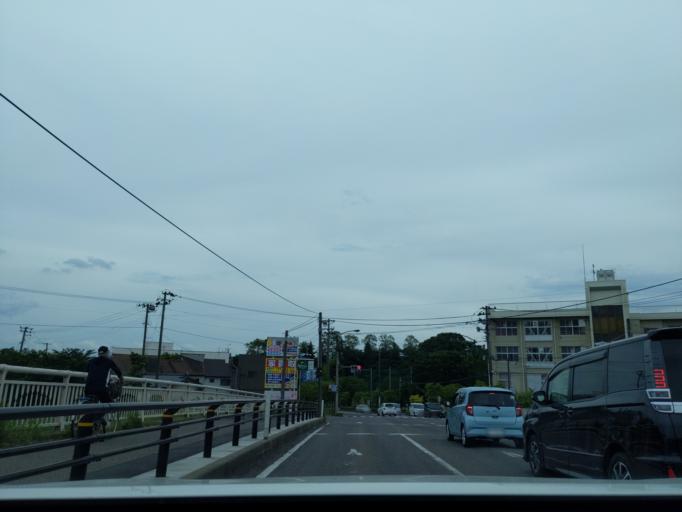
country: JP
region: Fukushima
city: Koriyama
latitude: 37.3663
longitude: 140.3632
